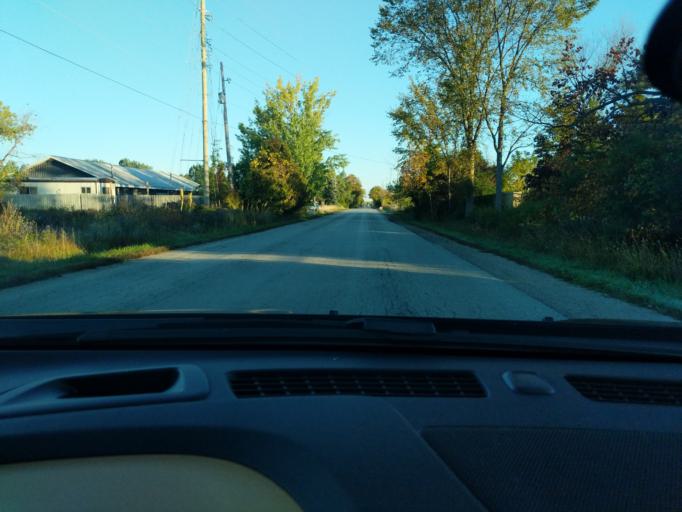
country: CA
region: Ontario
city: Collingwood
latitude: 44.4939
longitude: -80.2494
